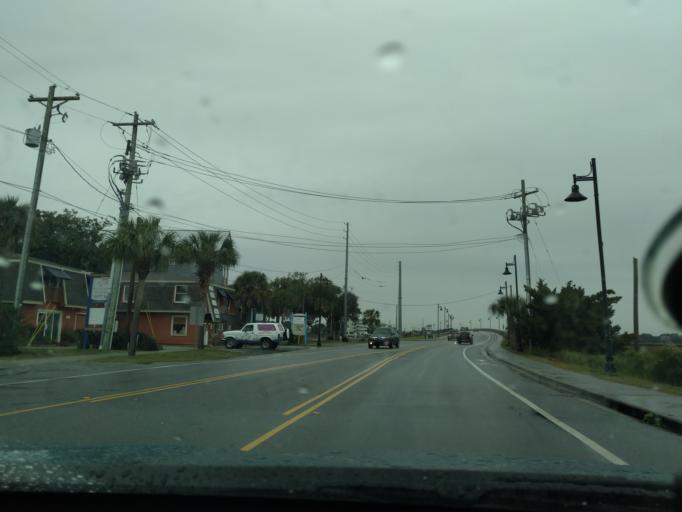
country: US
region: South Carolina
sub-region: Charleston County
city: Folly Beach
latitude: 32.6586
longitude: -79.9425
